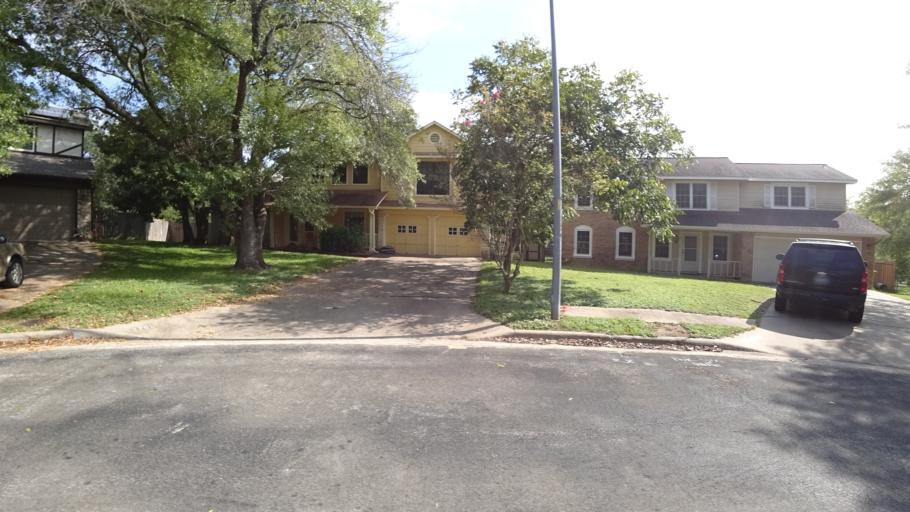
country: US
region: Texas
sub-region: Travis County
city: Shady Hollow
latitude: 30.2001
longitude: -97.8215
